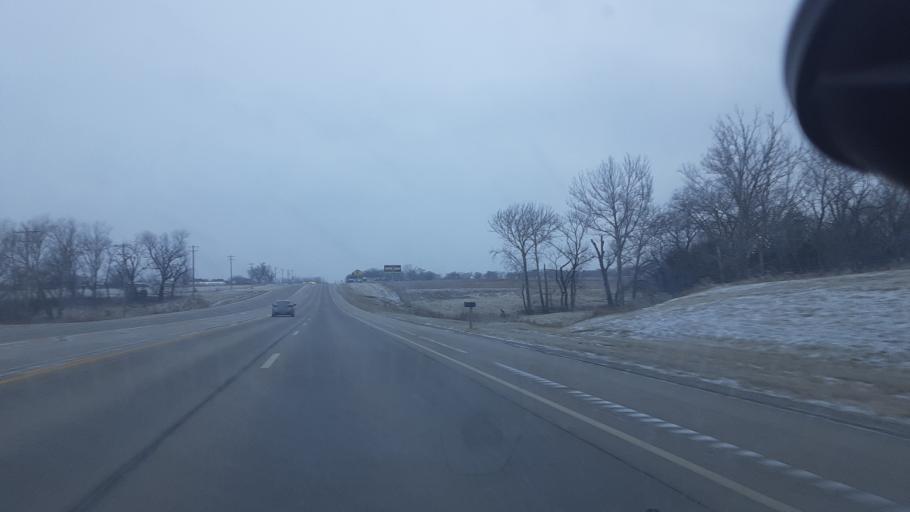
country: US
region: Oklahoma
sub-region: Payne County
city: Perkins
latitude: 35.9855
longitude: -97.0813
